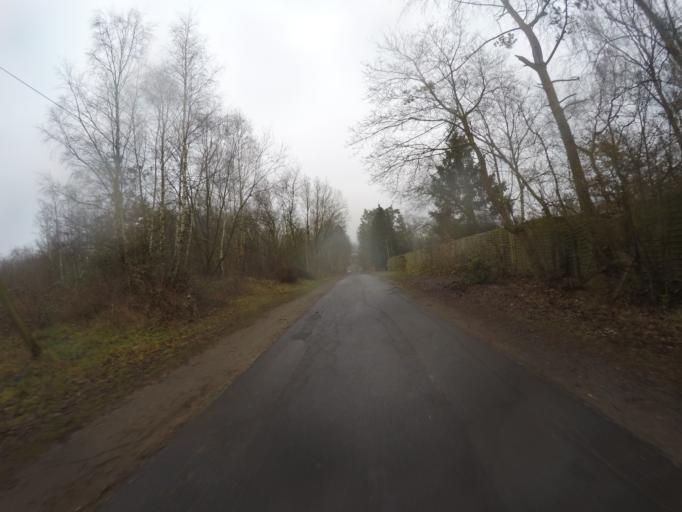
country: DE
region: Schleswig-Holstein
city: Quickborn
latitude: 53.7208
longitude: 9.9294
